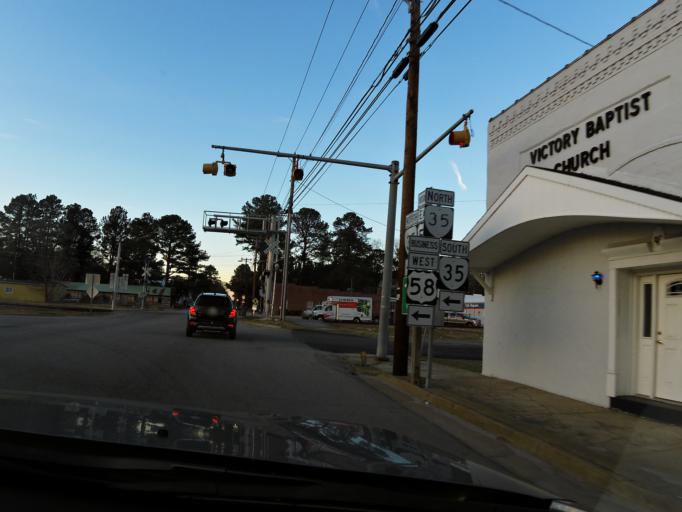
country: US
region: Virginia
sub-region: Southampton County
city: Courtland
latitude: 36.7174
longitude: -77.0685
